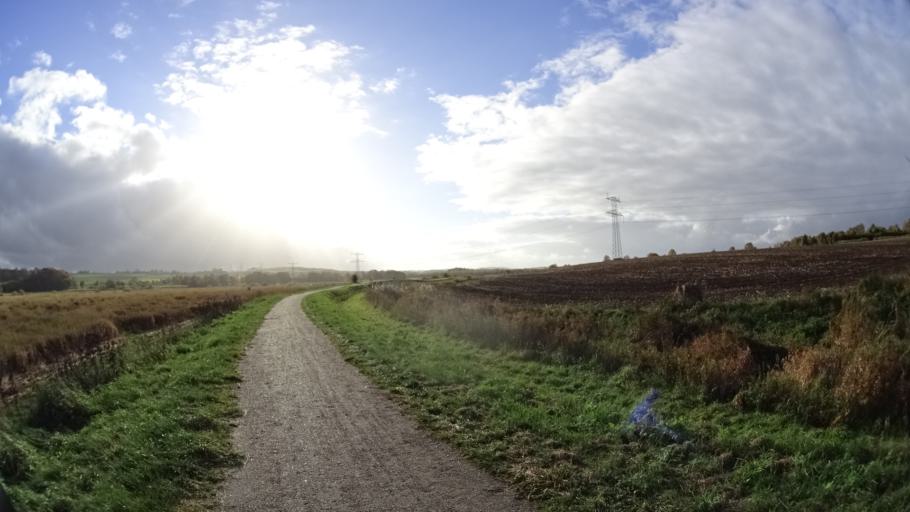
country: DK
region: Central Jutland
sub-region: Arhus Kommune
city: Kolt
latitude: 56.1364
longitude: 10.0499
